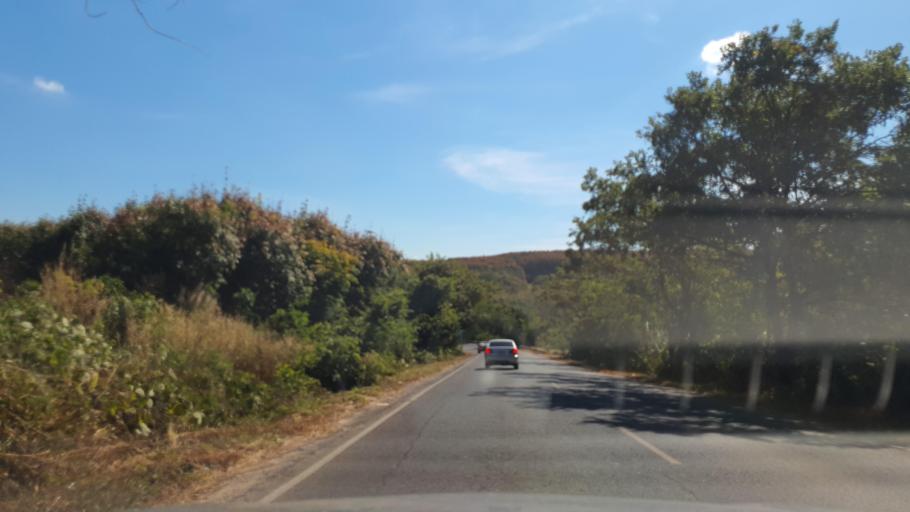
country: TH
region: Kalasin
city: Khao Wong
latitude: 16.7800
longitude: 104.1508
